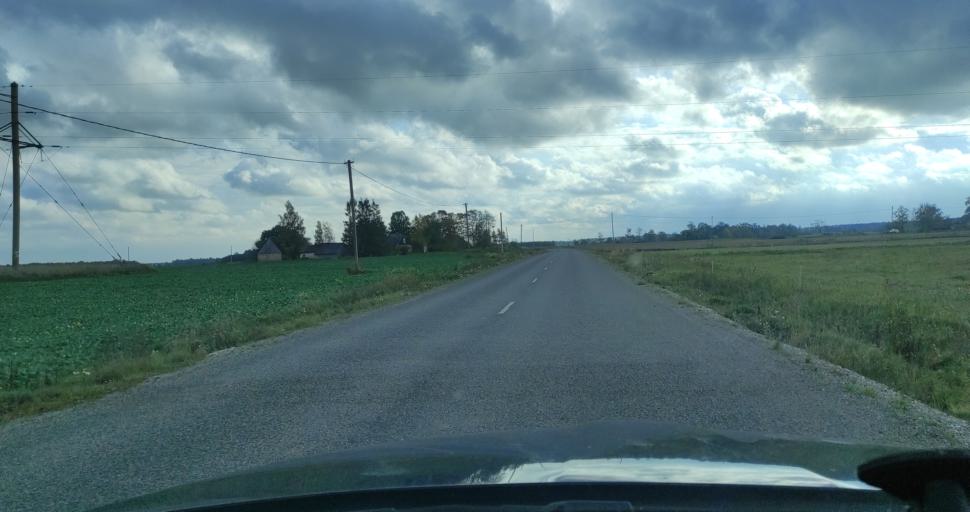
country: LV
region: Talsu Rajons
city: Sabile
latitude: 56.9388
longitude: 22.3965
